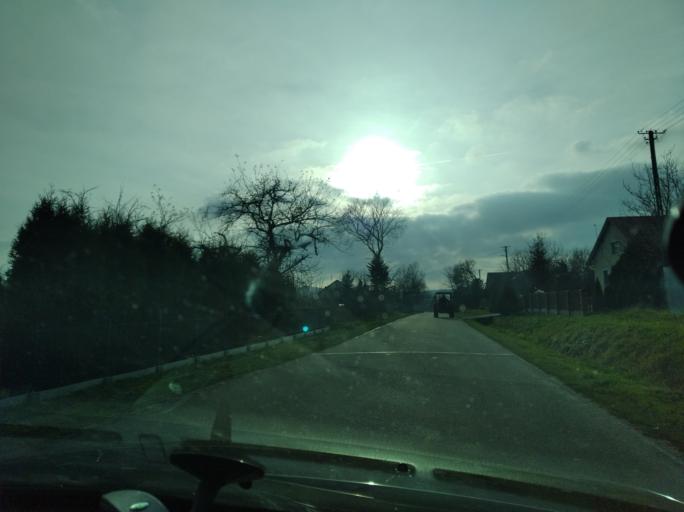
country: PL
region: Subcarpathian Voivodeship
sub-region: Powiat przeworski
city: Lopuszka Wielka
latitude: 49.9473
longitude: 22.4077
